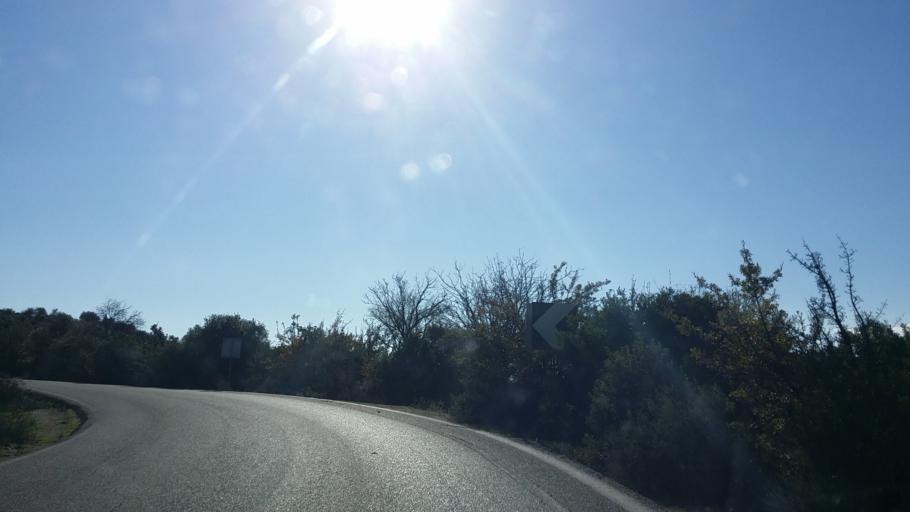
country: GR
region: West Greece
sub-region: Nomos Aitolias kai Akarnanias
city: Palairos
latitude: 38.7380
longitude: 20.8948
